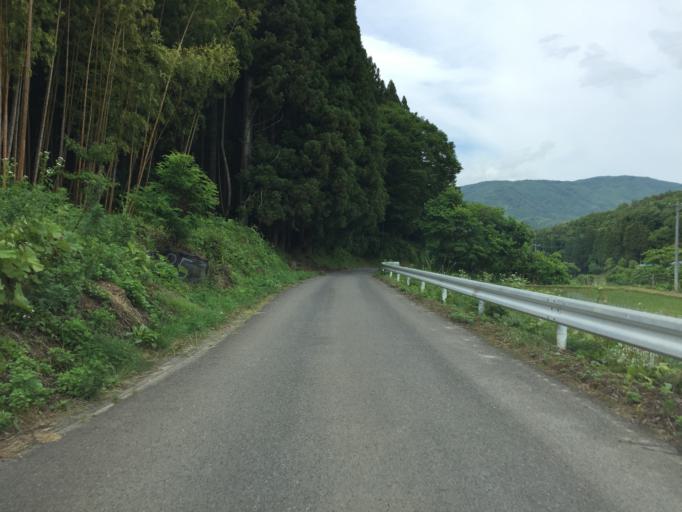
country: JP
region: Fukushima
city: Funehikimachi-funehiki
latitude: 37.5048
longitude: 140.6481
